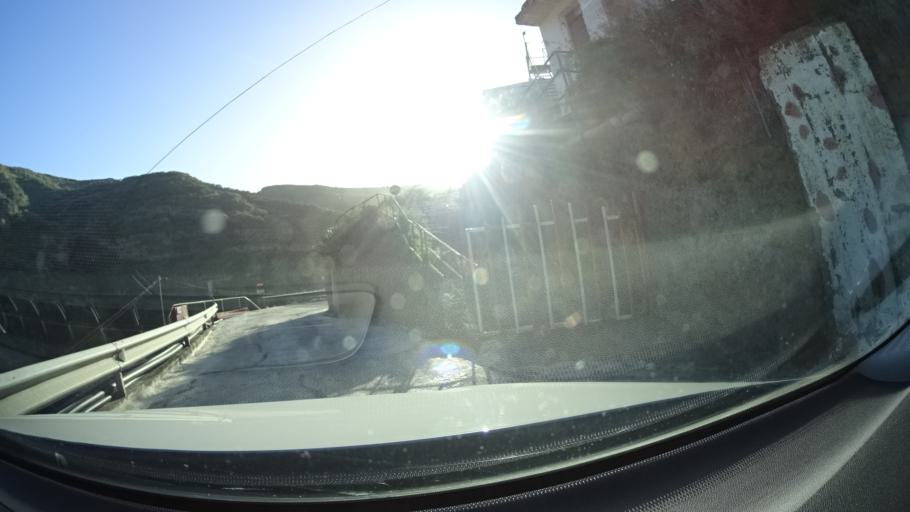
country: ES
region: Canary Islands
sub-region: Provincia de Las Palmas
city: Artenara
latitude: 28.0461
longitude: -15.6623
